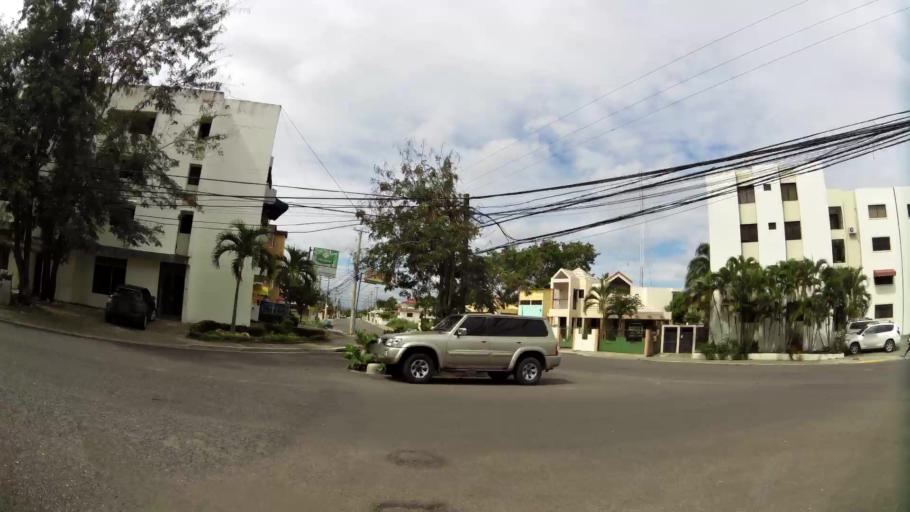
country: DO
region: Santiago
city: Santiago de los Caballeros
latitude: 19.4429
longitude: -70.6723
